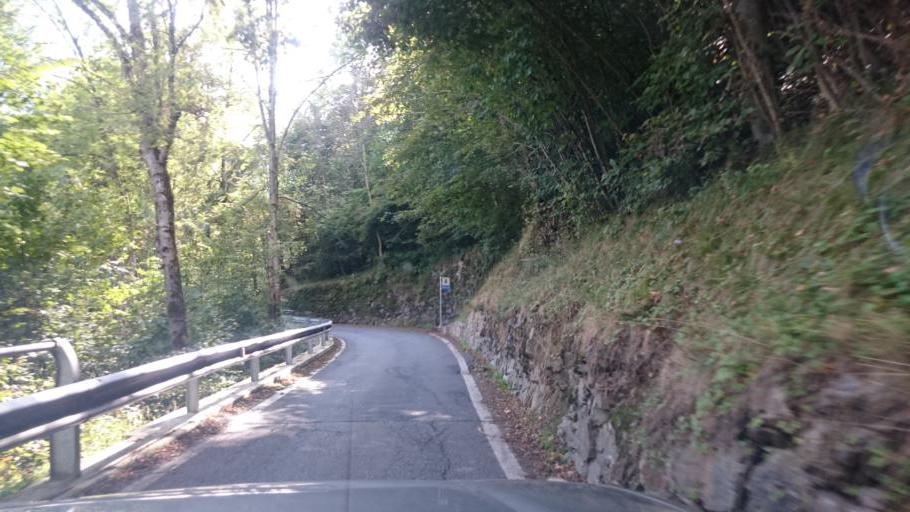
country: IT
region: Lombardy
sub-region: Provincia di Brescia
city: Paisco Loveno
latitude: 46.0729
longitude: 10.2785
